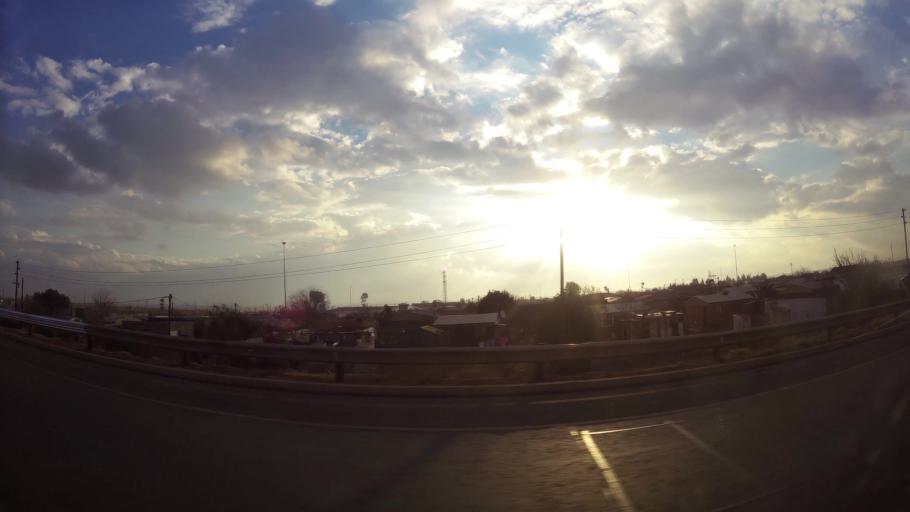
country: ZA
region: Gauteng
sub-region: Sedibeng District Municipality
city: Vanderbijlpark
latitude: -26.6037
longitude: 27.8175
